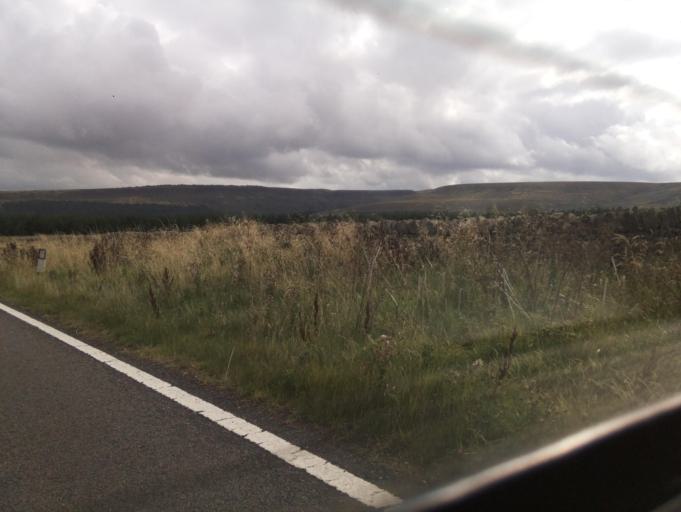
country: GB
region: England
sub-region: Kirklees
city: Meltham
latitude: 53.5423
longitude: -1.8461
